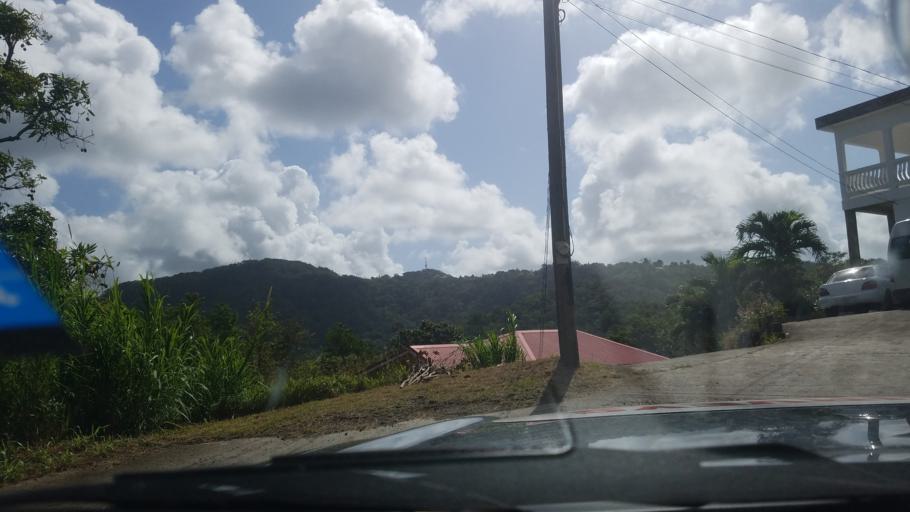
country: LC
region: Castries Quarter
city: Bisee
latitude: 14.0083
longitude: -60.9544
